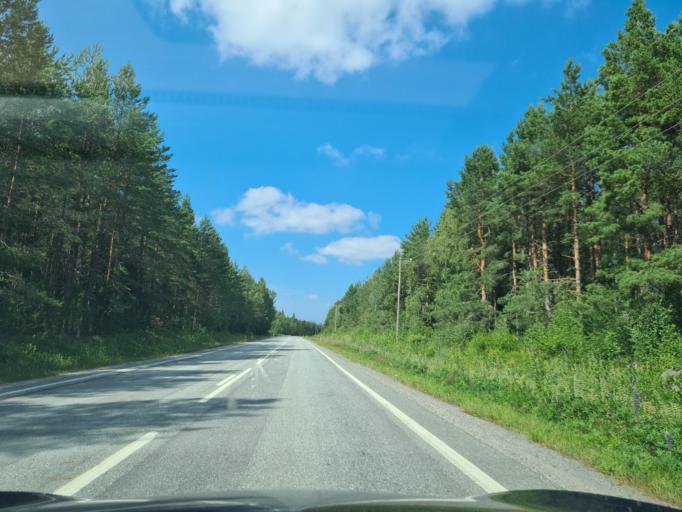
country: FI
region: Ostrobothnia
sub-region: Vaasa
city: Vaasa
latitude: 63.1805
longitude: 21.5729
